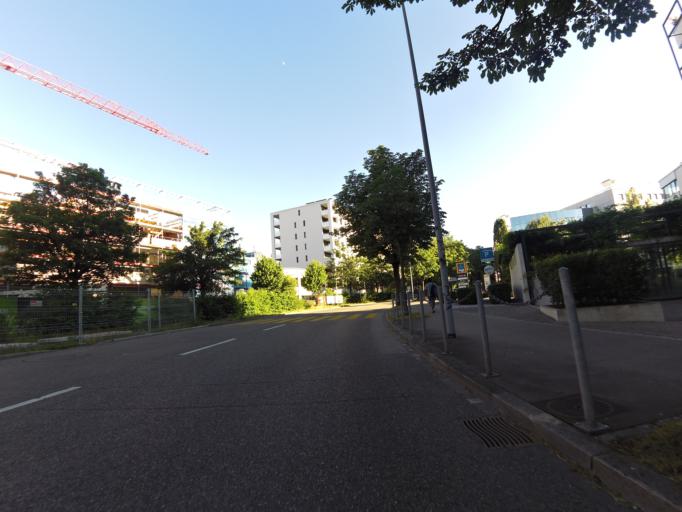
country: CH
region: Zurich
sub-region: Bezirk Zuerich
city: Zuerich (Kreis 9) / Altstetten
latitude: 47.3880
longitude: 8.4974
